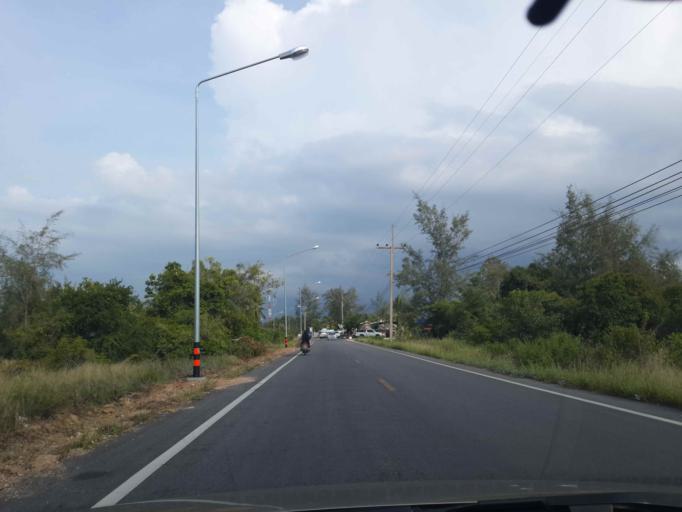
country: TH
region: Pattani
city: Yaring
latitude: 6.8994
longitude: 101.3639
